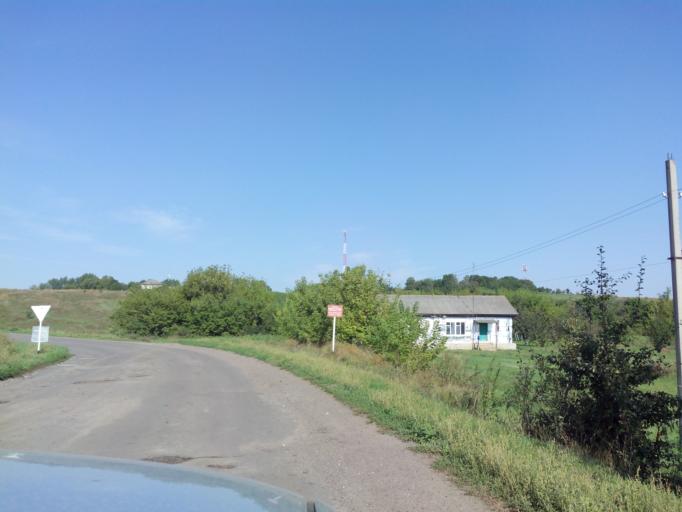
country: RU
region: Tambov
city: Zherdevka
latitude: 51.7278
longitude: 41.4676
